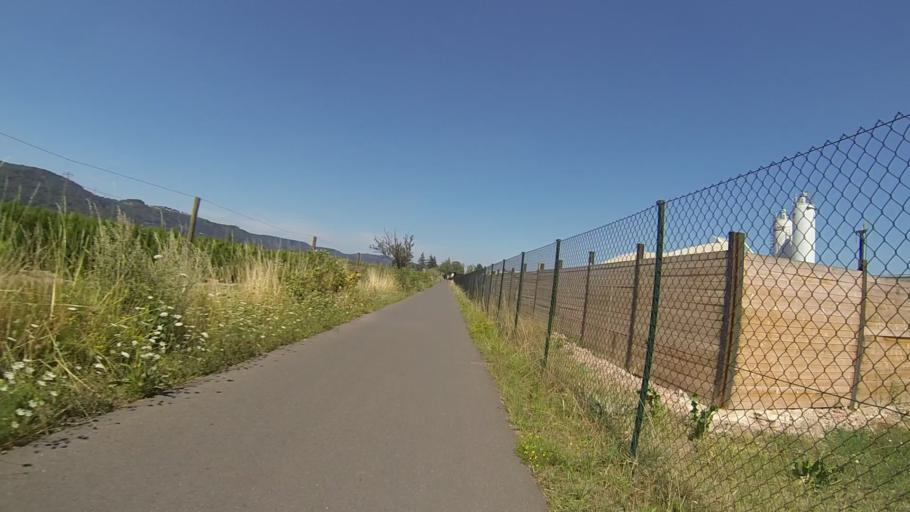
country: DE
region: Rheinland-Pfalz
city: Trier
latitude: 49.7291
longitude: 6.6202
